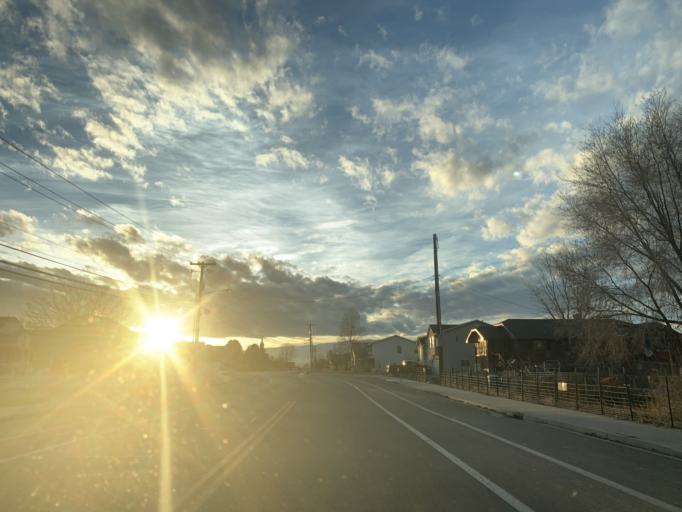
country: US
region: Utah
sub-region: Utah County
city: Provo
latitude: 40.2426
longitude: -111.7046
